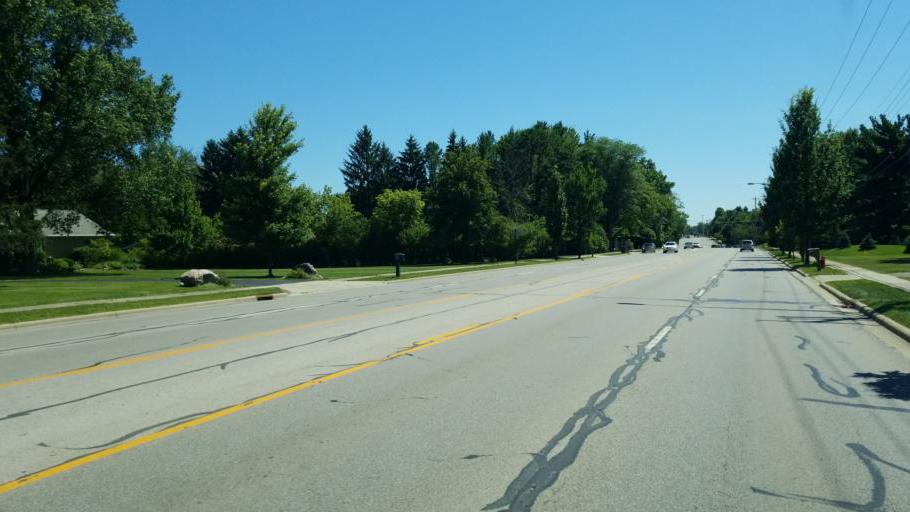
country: US
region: Ohio
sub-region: Franklin County
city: Huber Ridge
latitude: 40.0967
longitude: -82.8907
